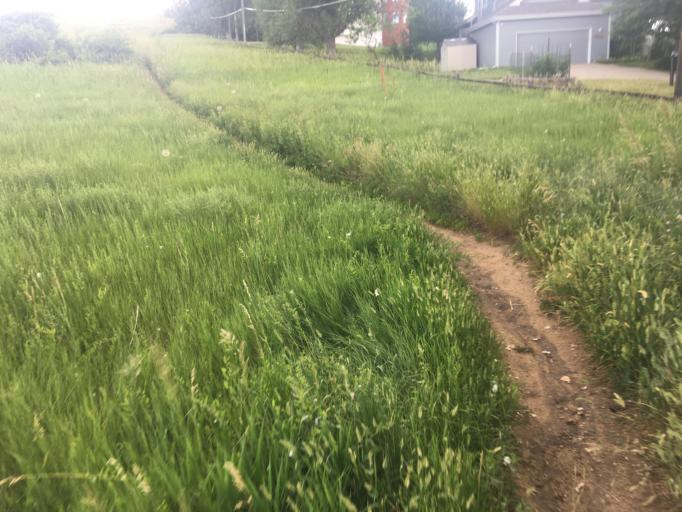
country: US
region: Colorado
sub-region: Boulder County
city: Superior
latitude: 39.9775
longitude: -105.1752
